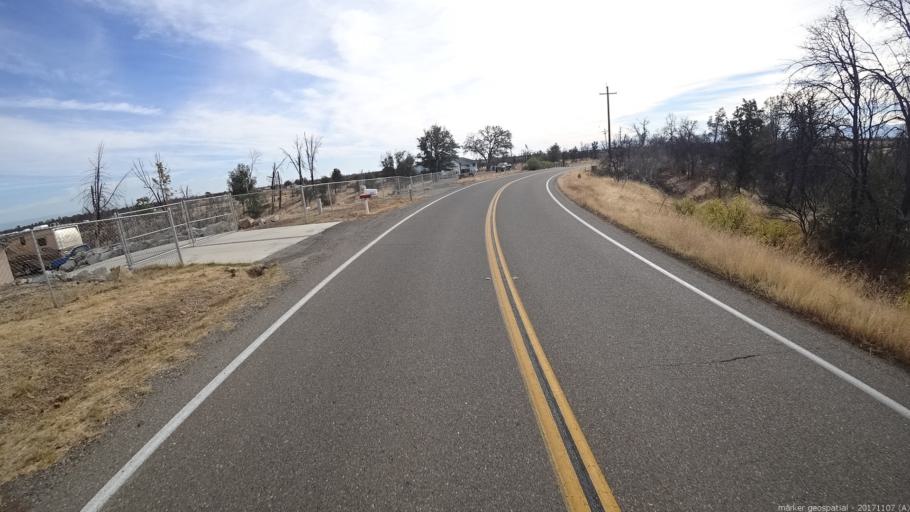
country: US
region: California
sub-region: Shasta County
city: Shasta
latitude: 40.4879
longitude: -122.5120
